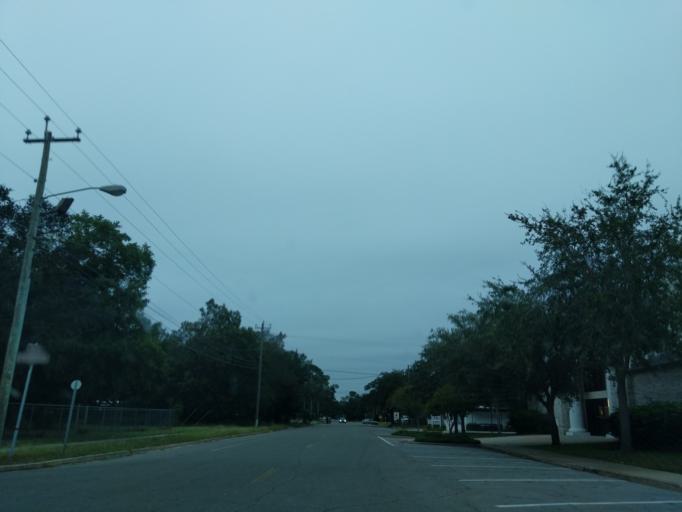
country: US
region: Florida
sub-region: Okaloosa County
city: Fort Walton Beach
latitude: 30.4053
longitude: -86.6099
